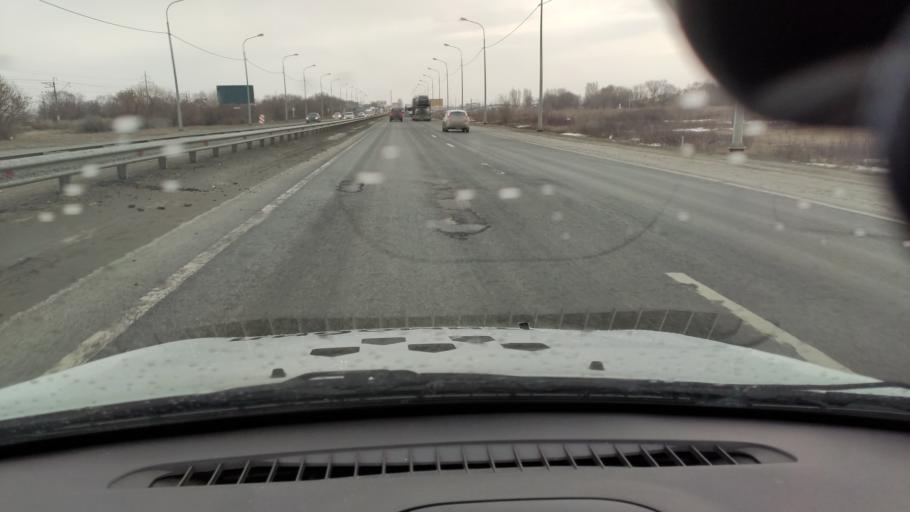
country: RU
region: Samara
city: Tol'yatti
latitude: 53.5734
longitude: 49.4564
